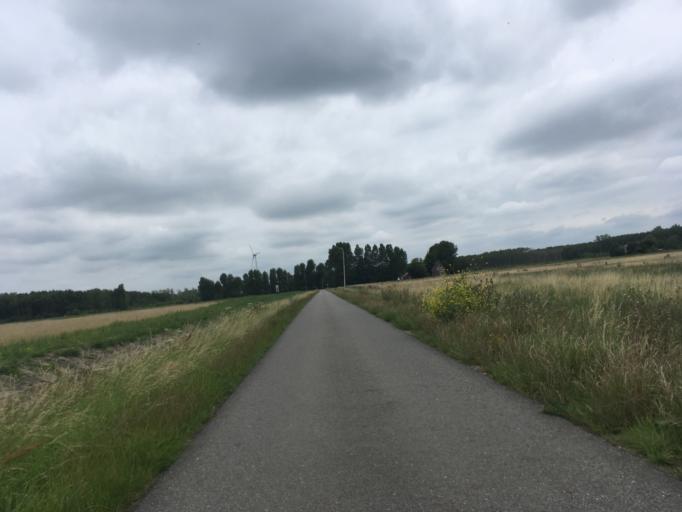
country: NL
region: North Holland
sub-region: Gemeente Velsen
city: Velsen-Zuid
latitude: 52.4210
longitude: 4.7247
